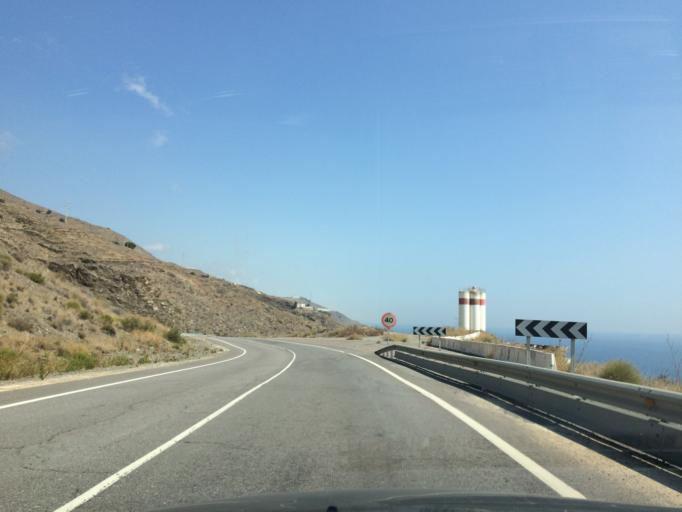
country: ES
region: Andalusia
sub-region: Provincia de Granada
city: Albunol
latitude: 36.7524
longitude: -3.1258
